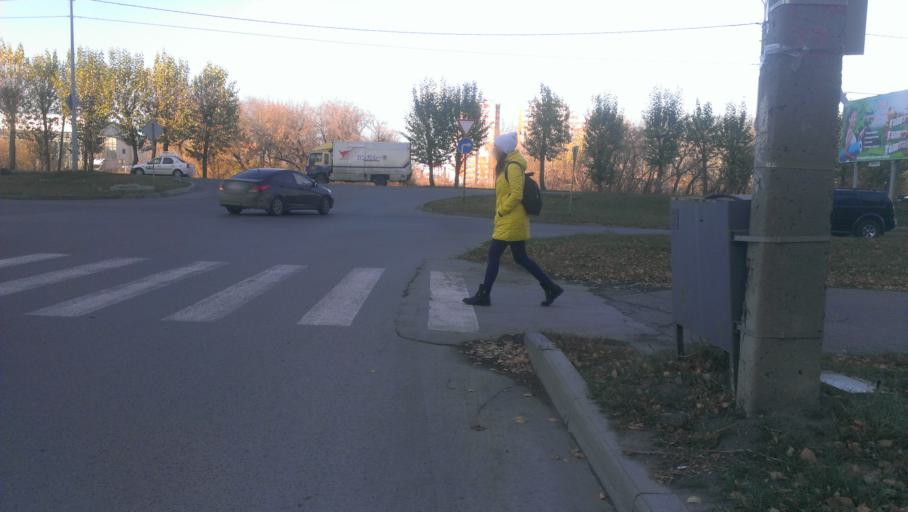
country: RU
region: Altai Krai
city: Novosilikatnyy
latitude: 53.3448
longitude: 83.6628
